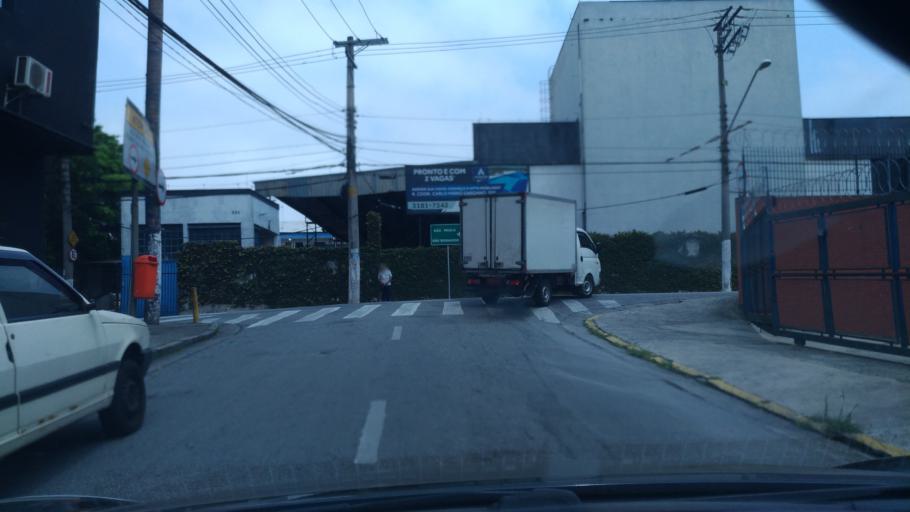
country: BR
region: Sao Paulo
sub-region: Sao Bernardo Do Campo
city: Sao Bernardo do Campo
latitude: -23.7180
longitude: -46.5555
